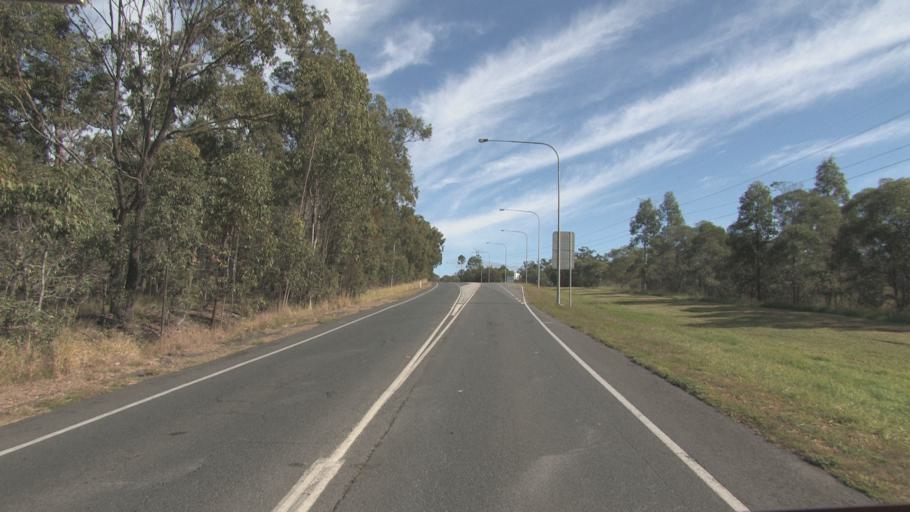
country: AU
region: Queensland
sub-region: Brisbane
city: Forest Lake
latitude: -27.6360
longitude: 152.9681
